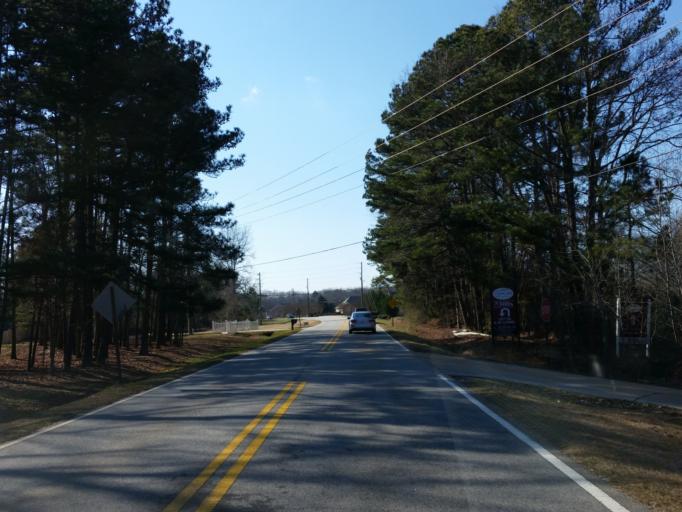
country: US
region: Georgia
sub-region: Clayton County
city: Lovejoy
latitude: 33.4416
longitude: -84.2518
